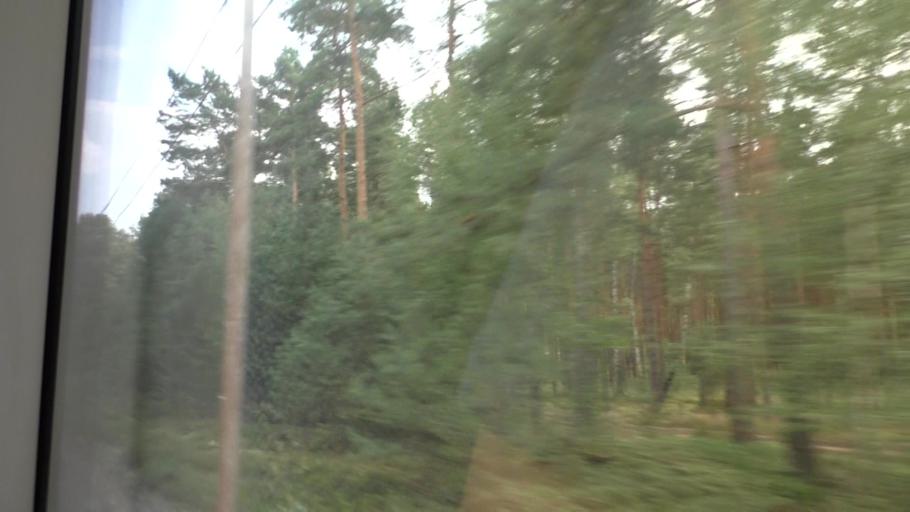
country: DE
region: Brandenburg
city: Reichenwalde
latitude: 52.2253
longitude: 13.9760
